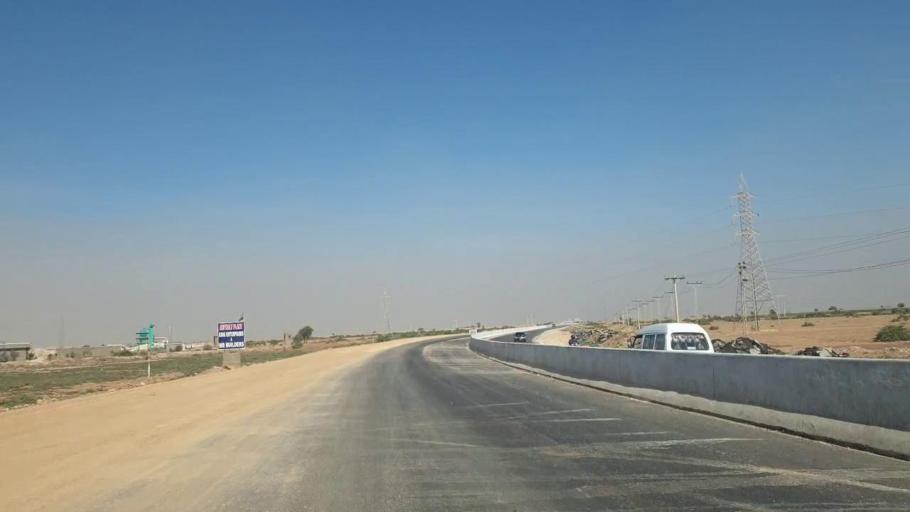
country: PK
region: Sindh
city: Jamshoro
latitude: 25.5204
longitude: 68.2743
